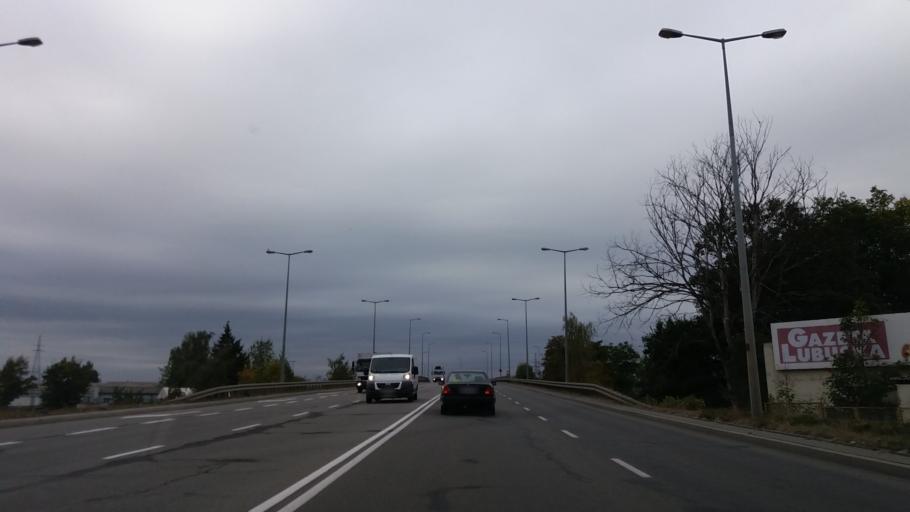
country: PL
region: Lubusz
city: Gorzow Wielkopolski
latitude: 52.7246
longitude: 15.2498
